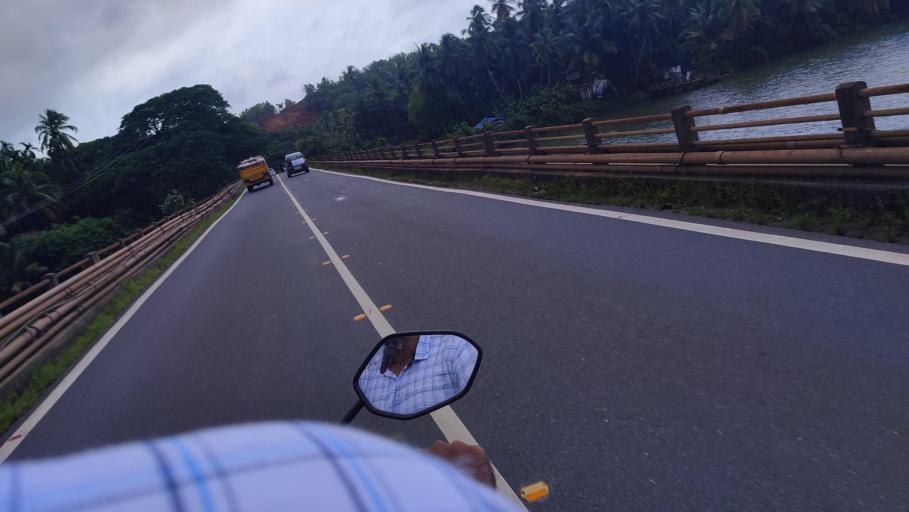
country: IN
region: Kerala
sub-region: Kasaragod District
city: Nileshwar
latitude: 12.2376
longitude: 75.1504
